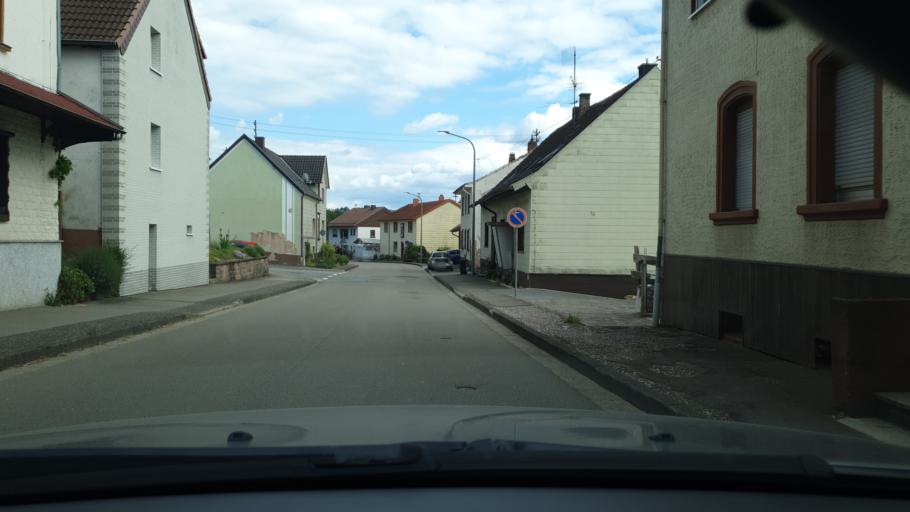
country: DE
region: Rheinland-Pfalz
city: Battweiler
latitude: 49.2771
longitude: 7.4634
